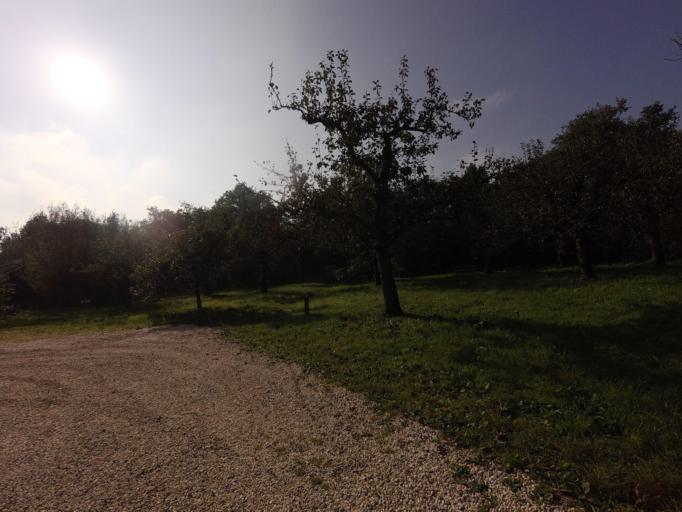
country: NL
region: Utrecht
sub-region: Gemeente Vianen
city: Vianen
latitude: 51.9597
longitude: 5.1118
